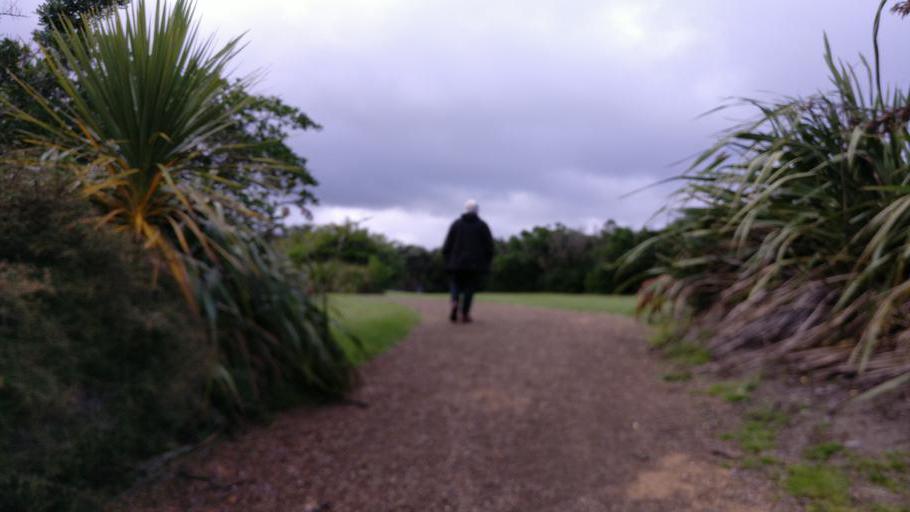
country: NZ
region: Wellington
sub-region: Lower Hutt City
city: Lower Hutt
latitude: -41.2364
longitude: 174.8987
